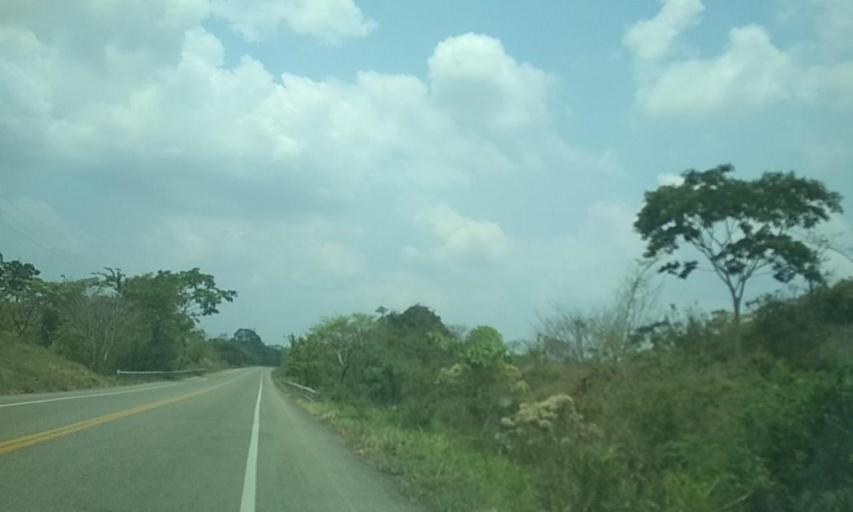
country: MX
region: Tabasco
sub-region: Huimanguillo
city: Francisco Rueda
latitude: 17.6476
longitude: -93.8319
